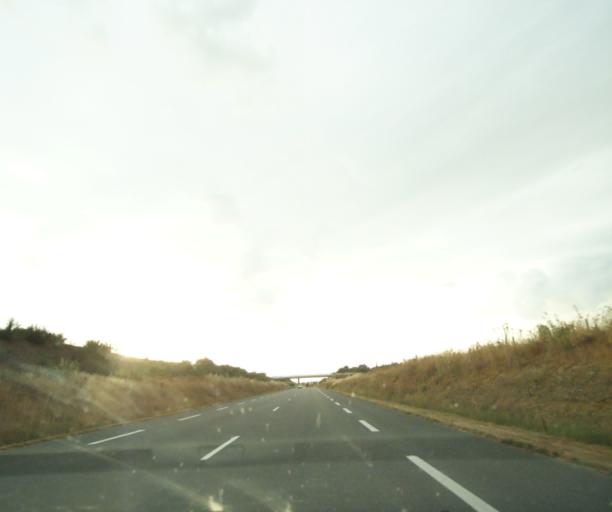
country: FR
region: Pays de la Loire
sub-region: Departement de la Vendee
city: Saint-Hilaire-de-Talmont
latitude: 46.4693
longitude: -1.6470
